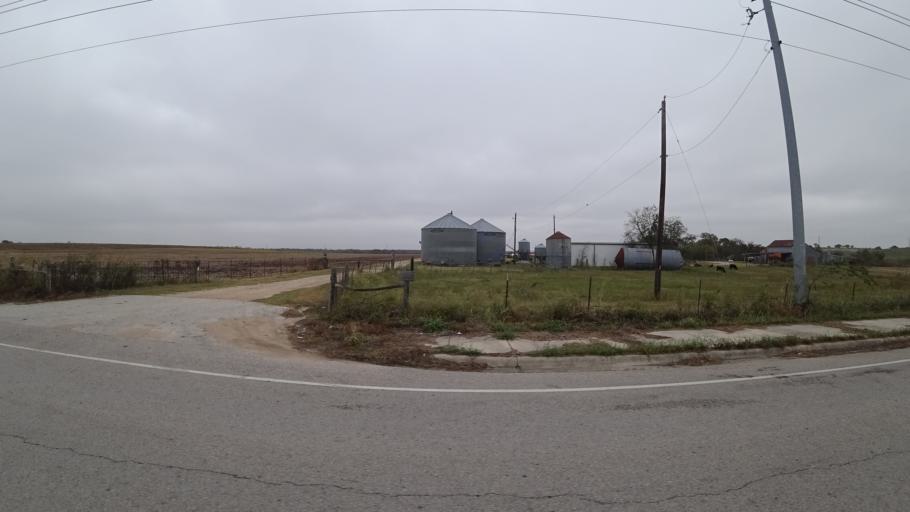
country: US
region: Texas
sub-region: Travis County
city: Pflugerville
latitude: 30.3858
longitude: -97.6007
